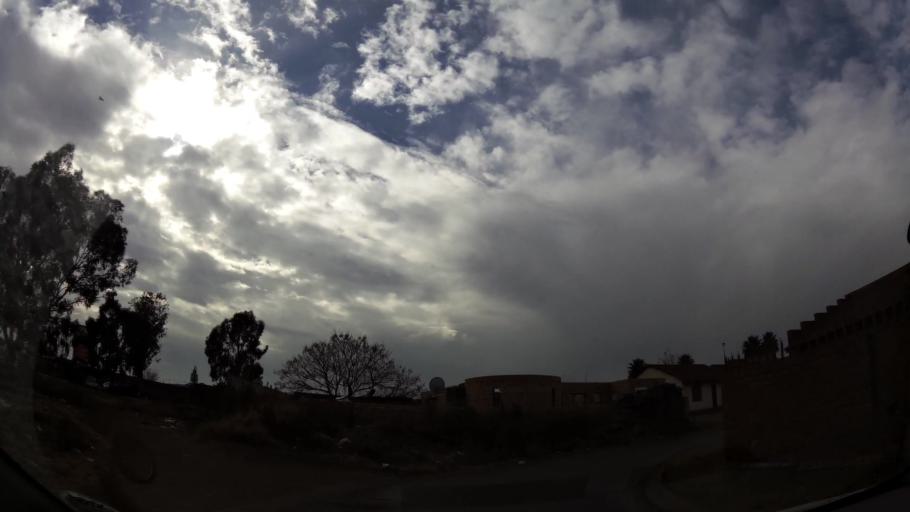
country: ZA
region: Gauteng
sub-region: Ekurhuleni Metropolitan Municipality
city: Germiston
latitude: -26.3273
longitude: 28.1832
